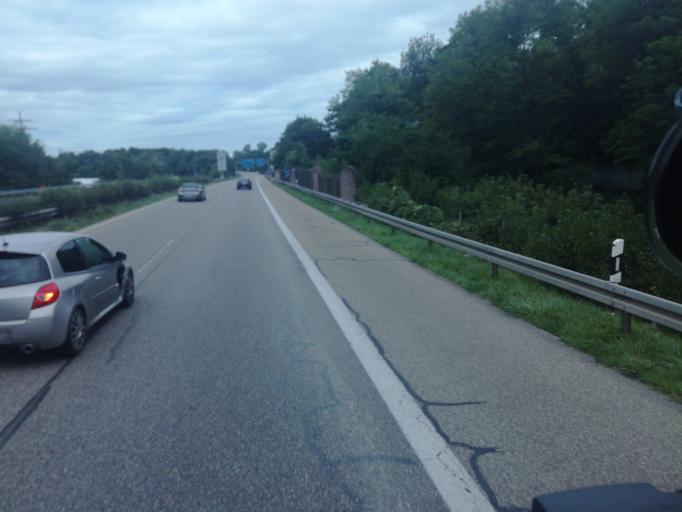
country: DE
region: Baden-Wuerttemberg
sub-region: Freiburg Region
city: Eimeldingen
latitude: 47.6216
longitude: 7.5904
